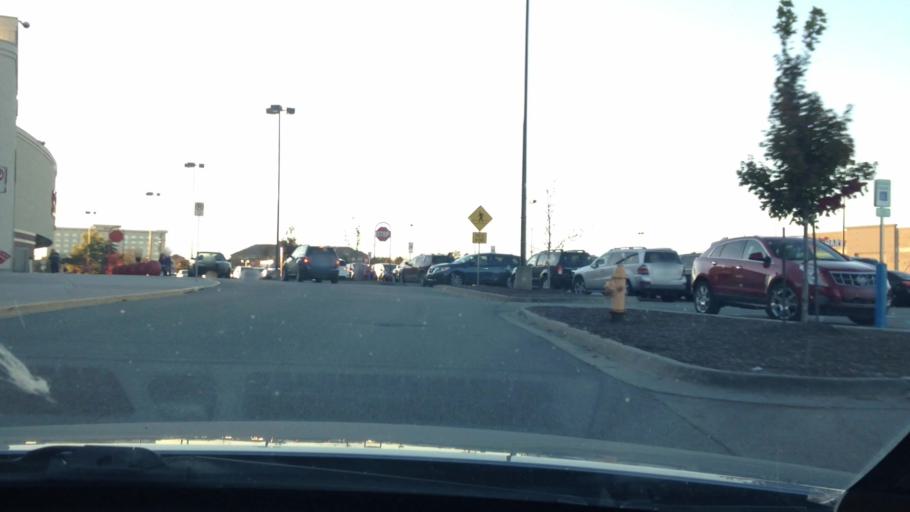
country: US
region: Kansas
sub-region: Johnson County
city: Lenexa
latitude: 38.9105
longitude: -94.7632
